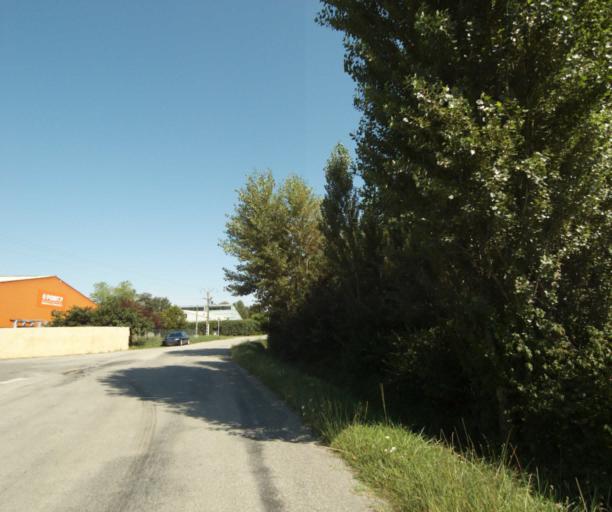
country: FR
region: Midi-Pyrenees
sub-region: Departement de l'Ariege
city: Lezat-sur-Leze
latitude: 43.2861
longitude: 1.3474
